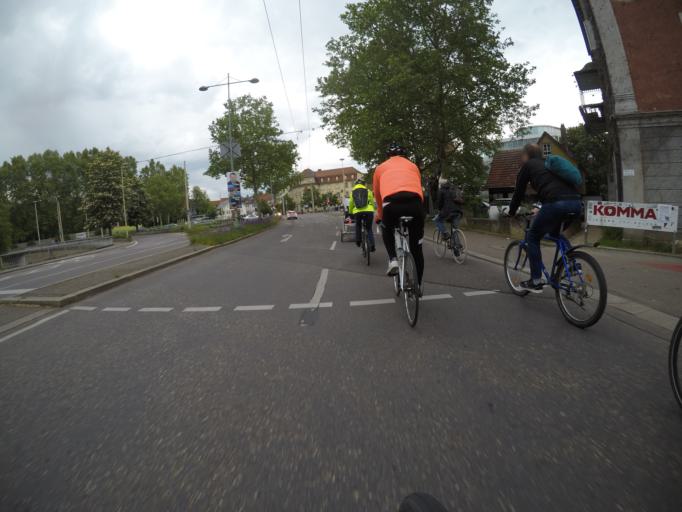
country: DE
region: Baden-Wuerttemberg
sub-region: Regierungsbezirk Stuttgart
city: Esslingen
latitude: 48.7384
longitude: 9.3090
